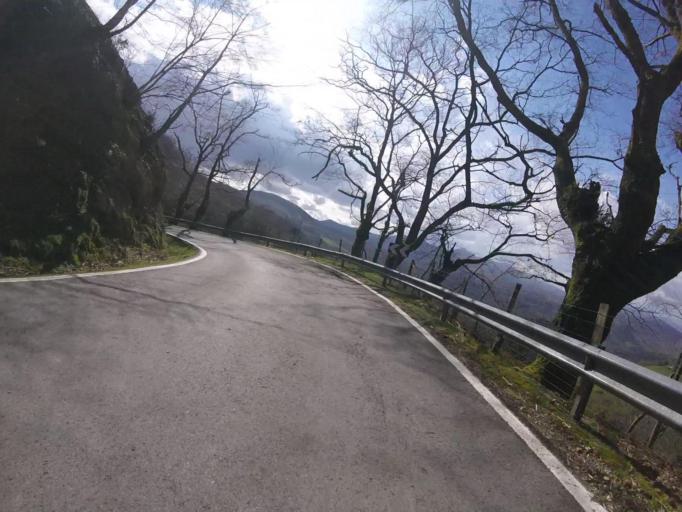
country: ES
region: Navarre
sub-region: Provincia de Navarra
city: Etxalar
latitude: 43.2549
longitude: -1.6172
